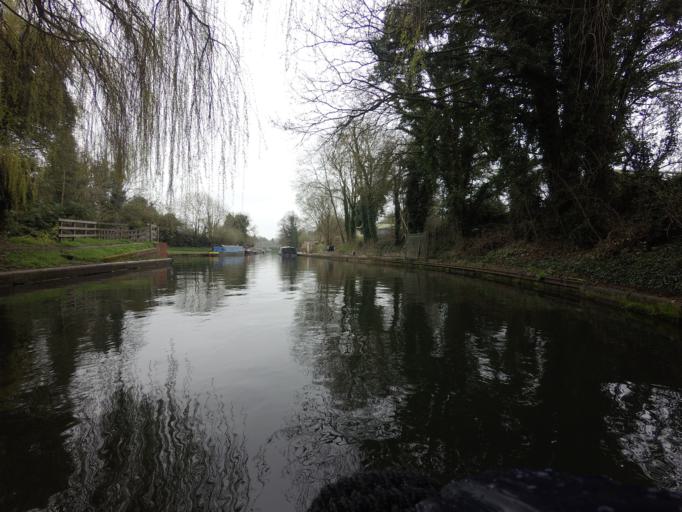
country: GB
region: England
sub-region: Hertfordshire
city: Kings Langley
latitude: 51.7274
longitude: -0.4523
